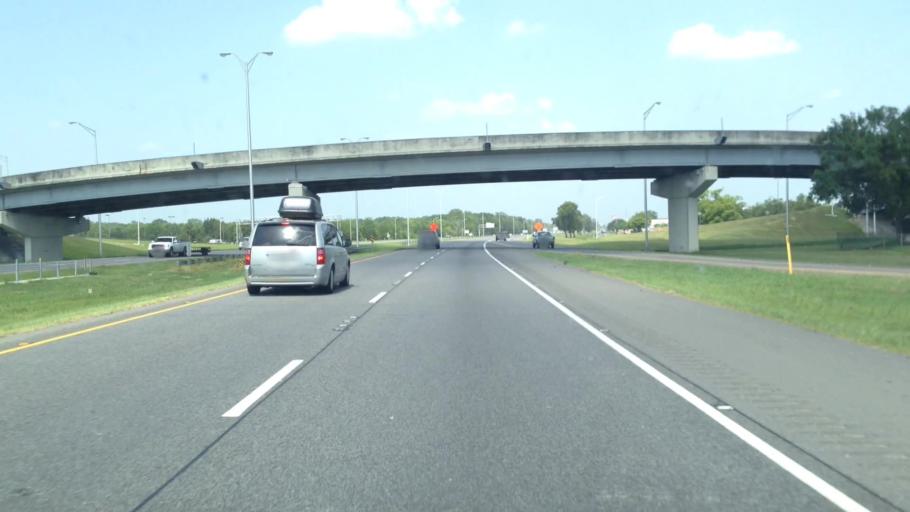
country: US
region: Louisiana
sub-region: Ouachita Parish
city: Lakeshore
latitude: 32.4947
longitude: -92.0556
